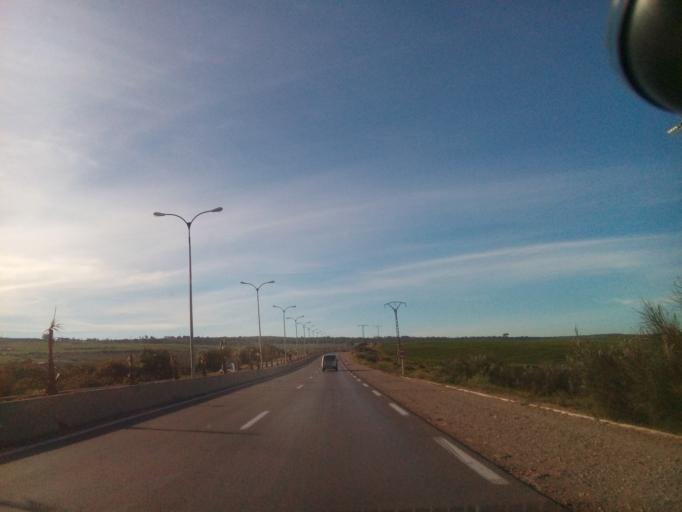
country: DZ
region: Mostaganem
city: Mostaganem
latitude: 35.8290
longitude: -0.0113
